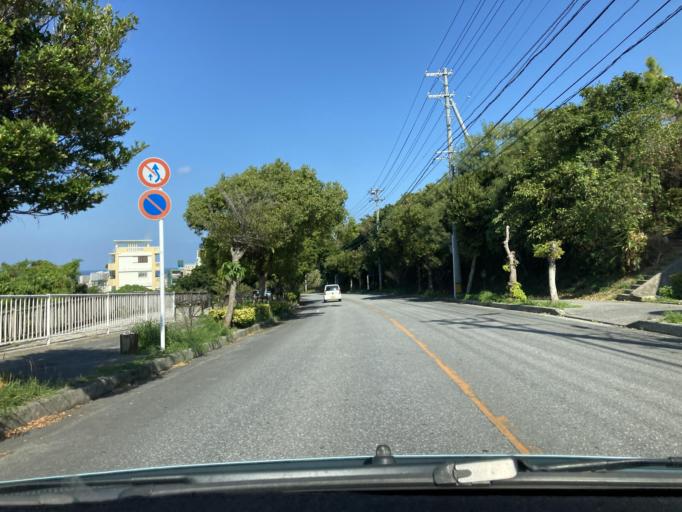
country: JP
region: Okinawa
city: Ginowan
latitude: 26.2515
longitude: 127.7259
